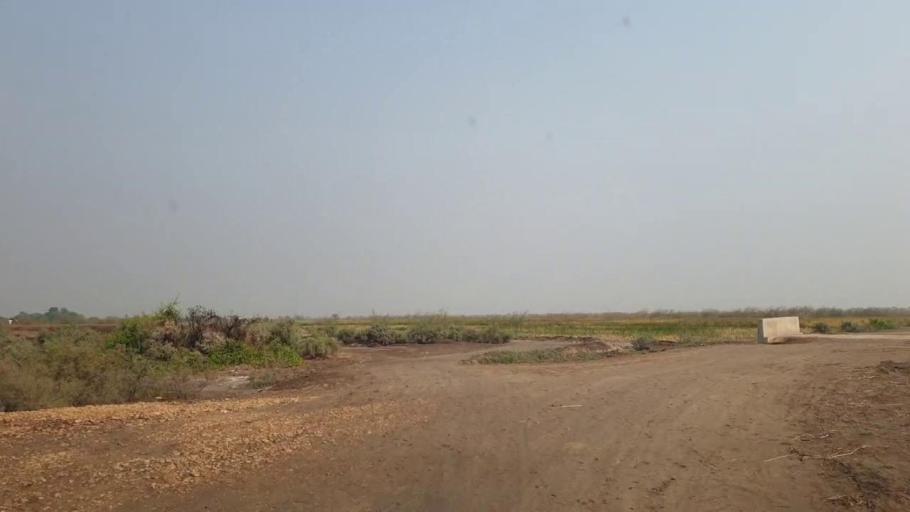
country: PK
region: Sindh
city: Matli
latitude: 25.1015
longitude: 68.6794
